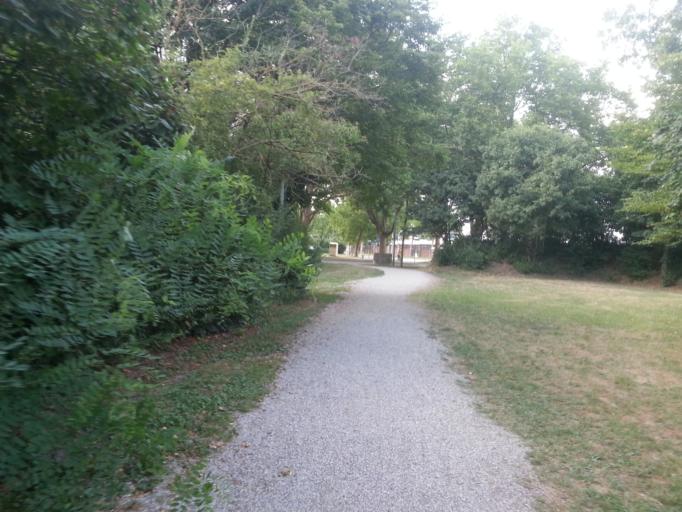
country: DE
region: Baden-Wuerttemberg
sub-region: Karlsruhe Region
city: Mannheim
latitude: 49.4642
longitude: 8.4750
